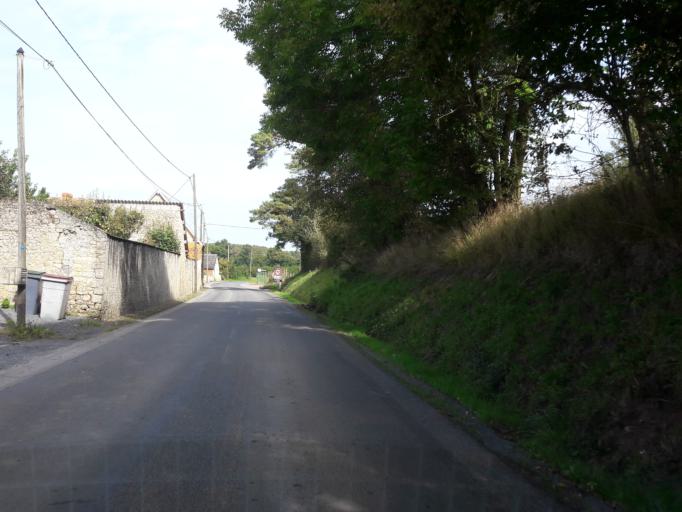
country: FR
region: Lower Normandy
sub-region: Departement du Calvados
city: Bayeux
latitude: 49.2248
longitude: -0.7064
